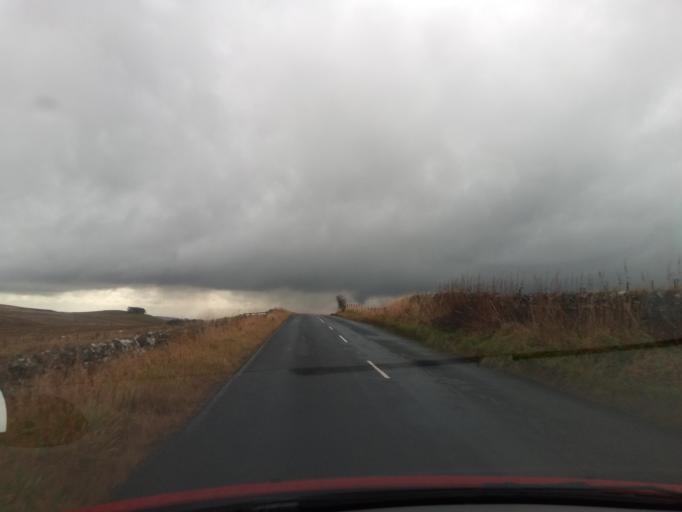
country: GB
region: England
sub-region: Northumberland
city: Corsenside
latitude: 55.1735
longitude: -2.2586
